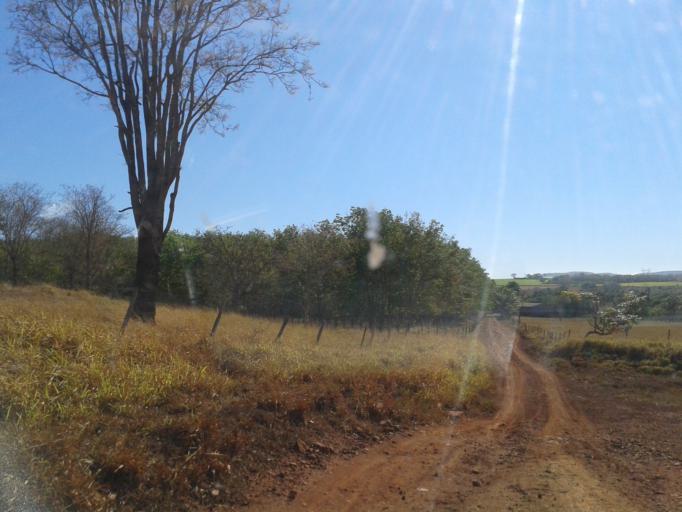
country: BR
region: Minas Gerais
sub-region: Centralina
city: Centralina
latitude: -18.5699
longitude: -49.1345
